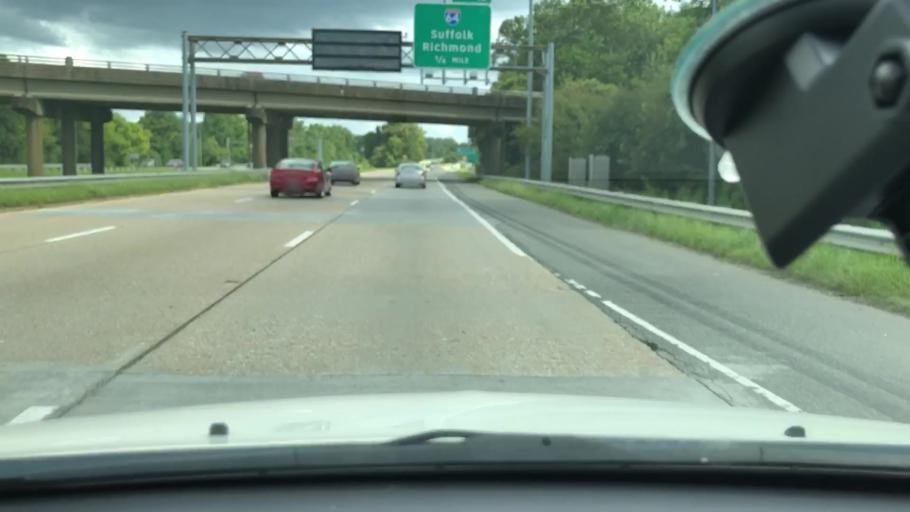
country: US
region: Virginia
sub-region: City of Chesapeake
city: Chesapeake
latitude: 36.7700
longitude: -76.2734
